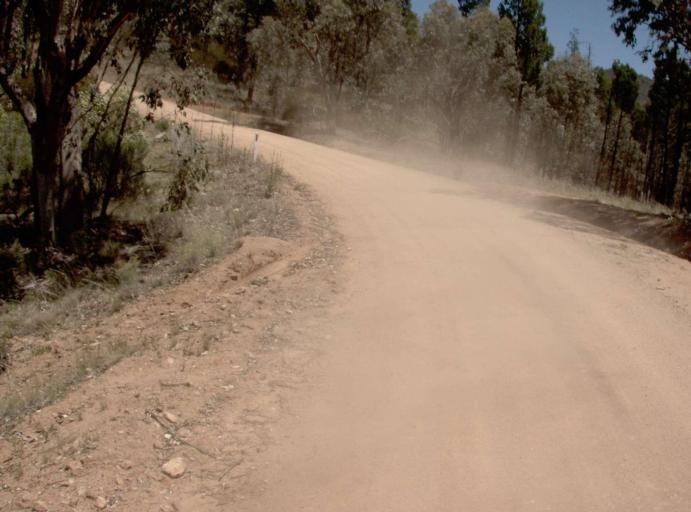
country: AU
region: New South Wales
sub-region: Snowy River
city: Jindabyne
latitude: -36.9255
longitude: 148.3770
